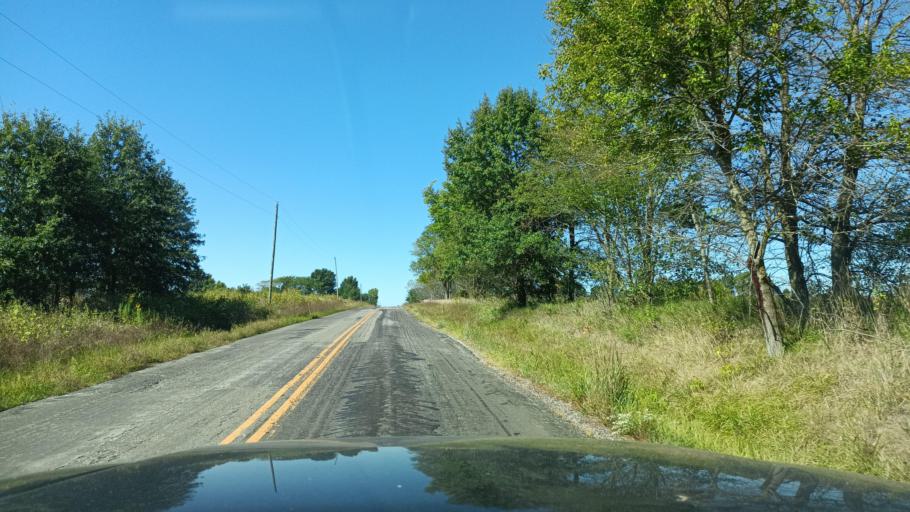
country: US
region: Missouri
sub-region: Scotland County
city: Memphis
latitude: 40.3549
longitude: -92.2224
